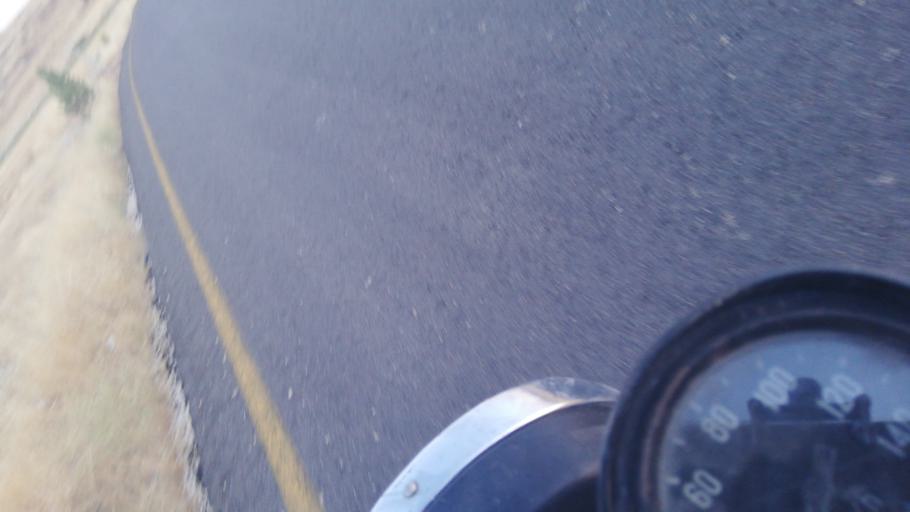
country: TR
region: Mardin
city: Kindirip
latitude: 37.4724
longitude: 41.2280
